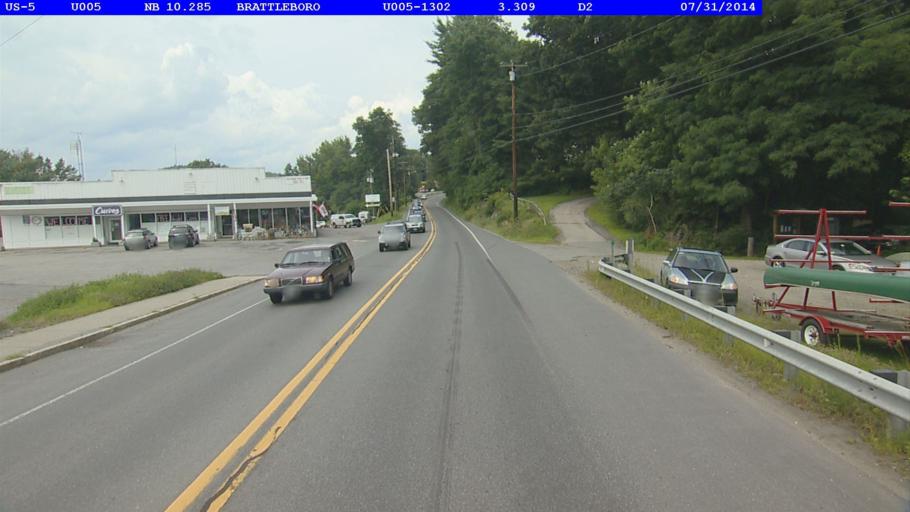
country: US
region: Vermont
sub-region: Windham County
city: Brattleboro
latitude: 42.8670
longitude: -72.5565
